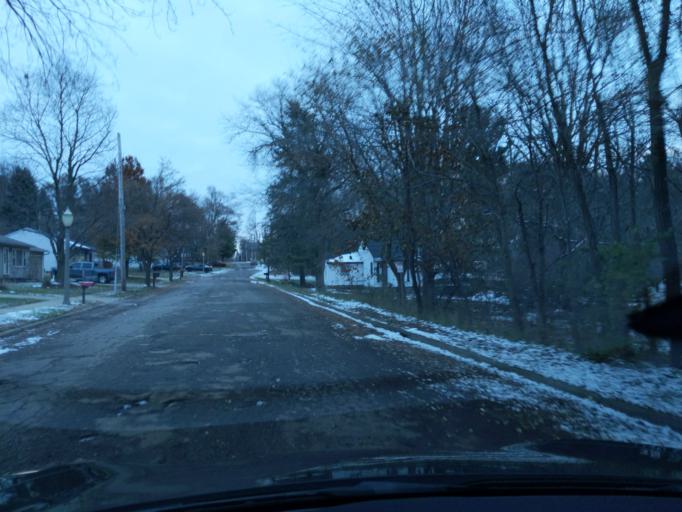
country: US
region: Michigan
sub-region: Ingham County
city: Lansing
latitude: 42.7657
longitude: -84.5494
